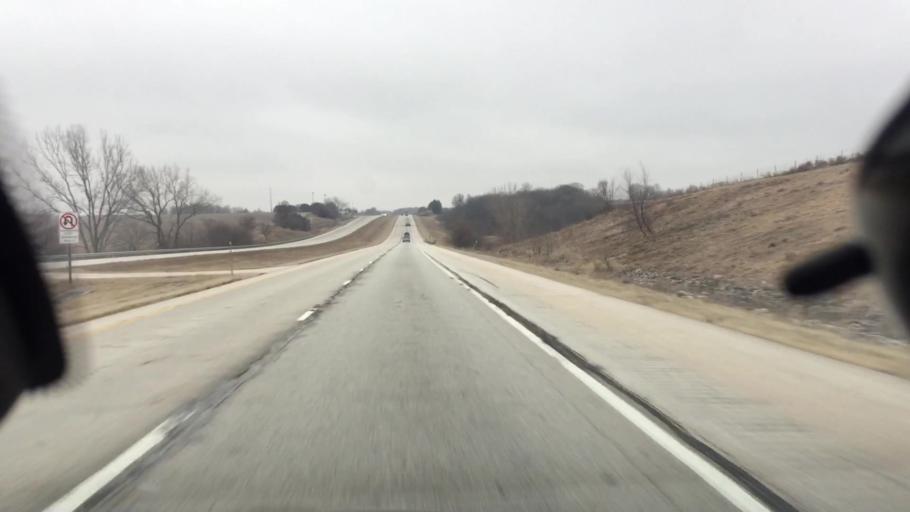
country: US
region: Illinois
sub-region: Henry County
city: Orion
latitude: 41.2244
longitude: -90.3320
